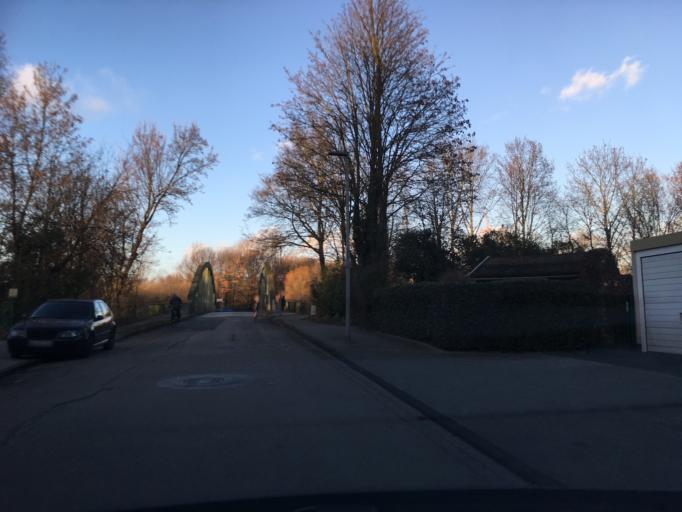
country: DE
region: North Rhine-Westphalia
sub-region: Regierungsbezirk Munster
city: Bottrop
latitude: 51.4937
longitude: 6.9114
